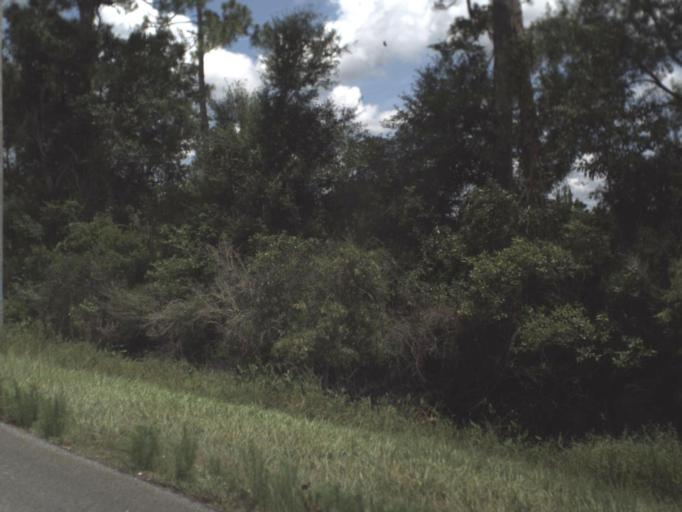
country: US
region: Florida
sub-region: Taylor County
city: Perry
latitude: 30.0988
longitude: -83.6930
